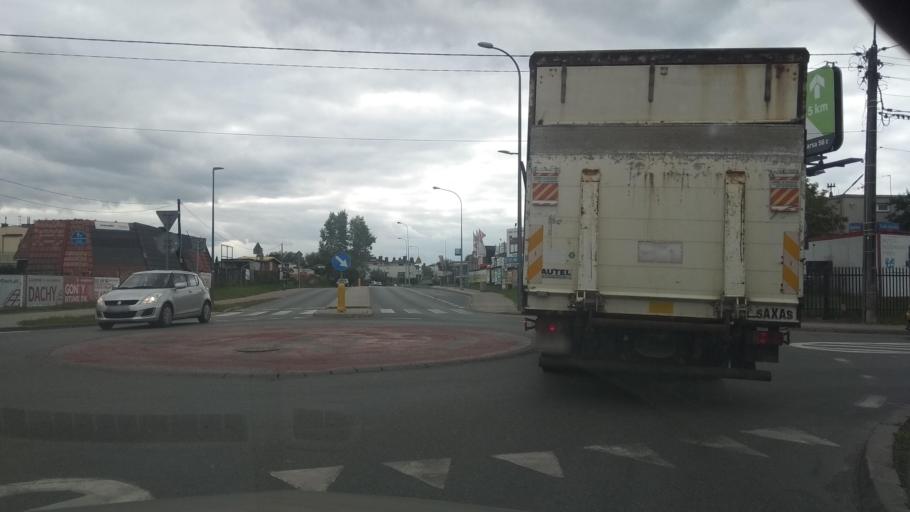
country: PL
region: Masovian Voivodeship
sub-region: Warszawa
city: Wawer
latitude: 52.2143
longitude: 21.1330
